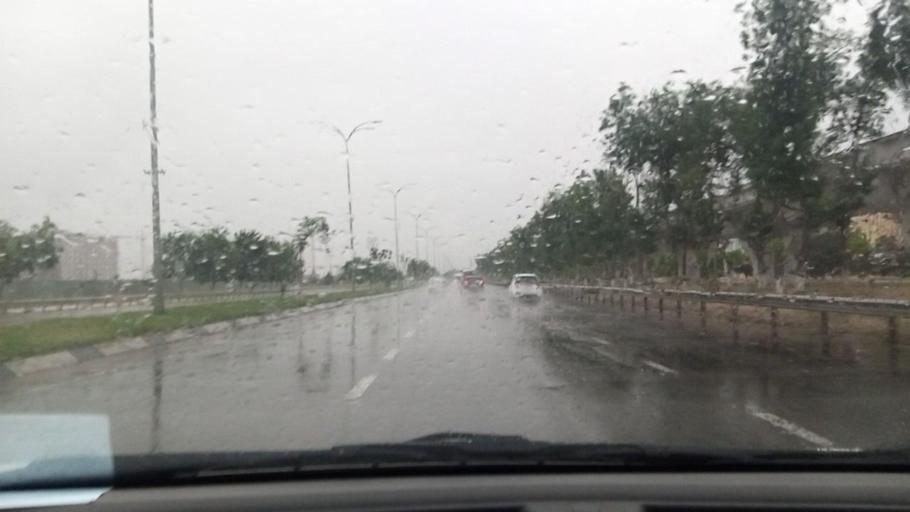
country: UZ
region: Toshkent Shahri
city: Bektemir
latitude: 41.2800
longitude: 69.3609
